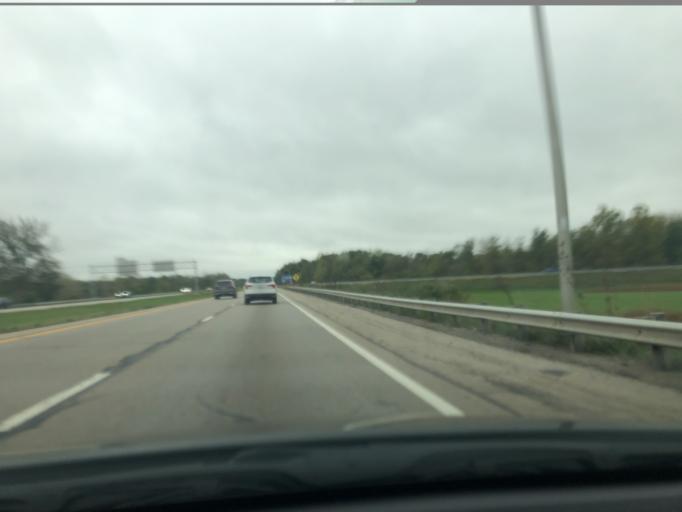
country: US
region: Ohio
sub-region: Union County
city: Marysville
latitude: 40.2521
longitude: -83.3648
